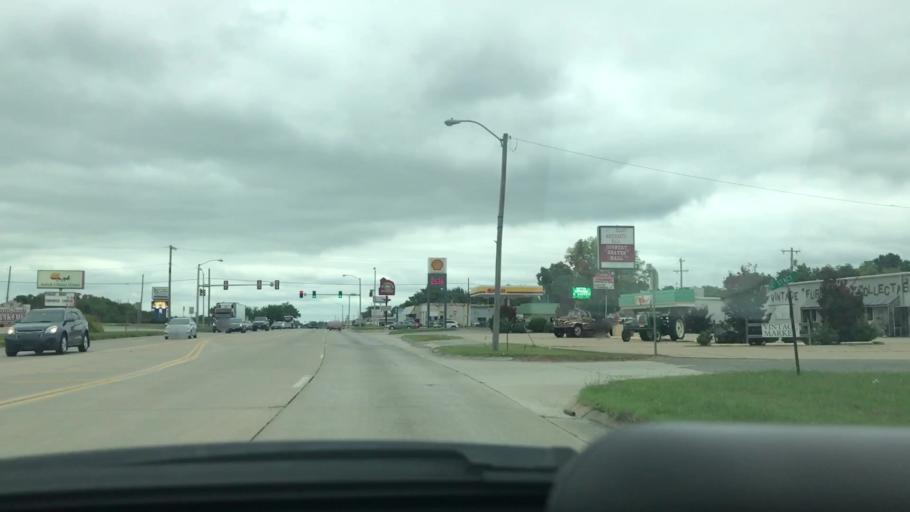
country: US
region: Oklahoma
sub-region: Mayes County
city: Chouteau
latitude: 36.1851
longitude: -95.3428
